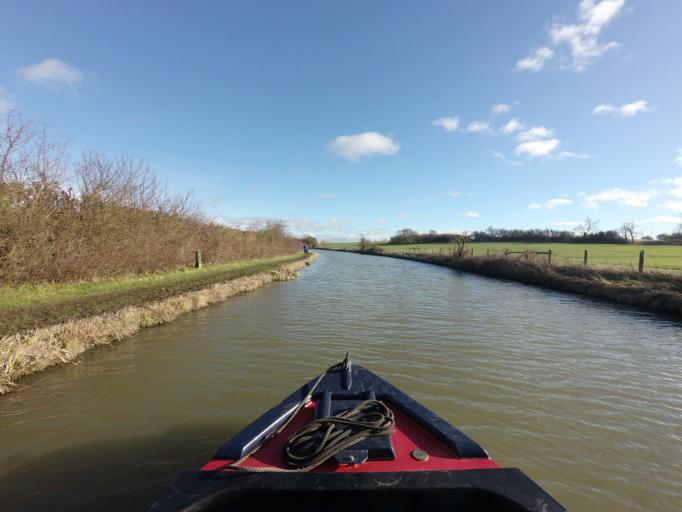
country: GB
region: England
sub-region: Northamptonshire
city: Bugbrooke
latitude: 52.2124
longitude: -1.0355
